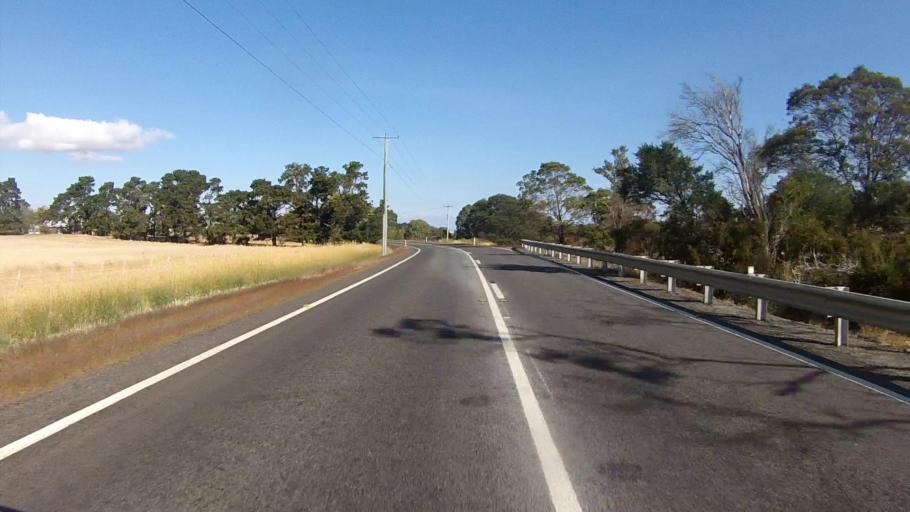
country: AU
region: Tasmania
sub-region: Sorell
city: Sorell
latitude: -42.7265
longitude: 147.5226
